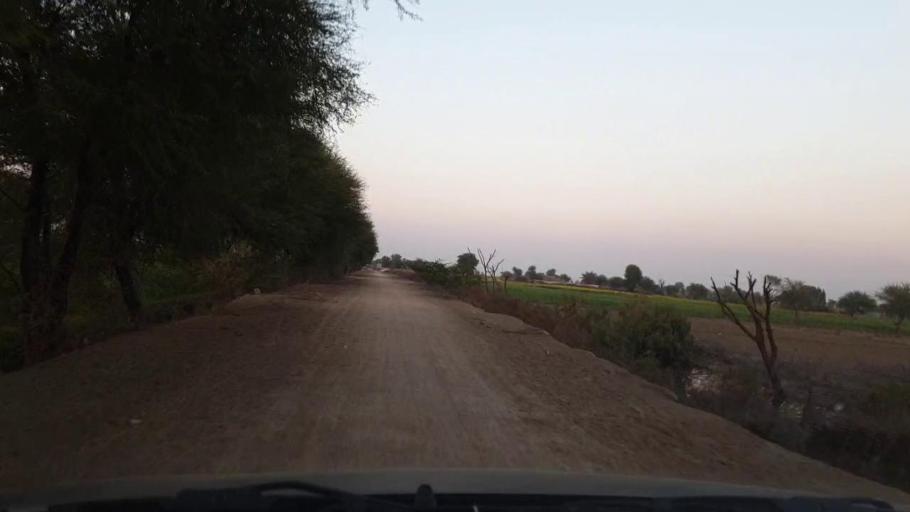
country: PK
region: Sindh
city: Jhol
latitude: 25.9371
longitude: 68.9685
